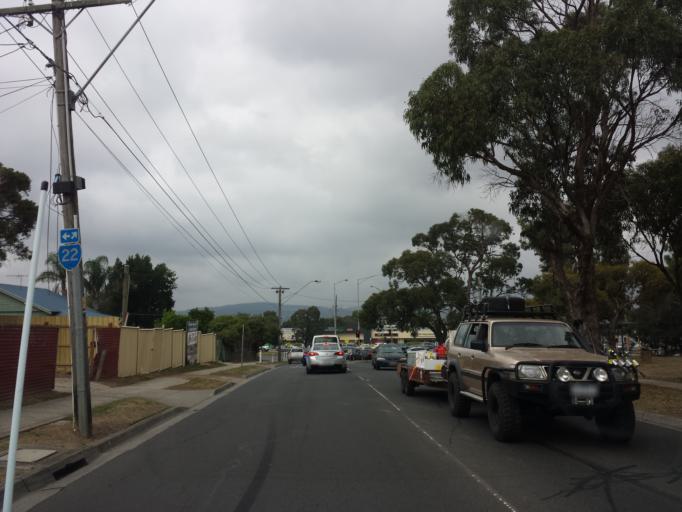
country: AU
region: Victoria
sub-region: Knox
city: Boronia
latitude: -37.8817
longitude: 145.2779
